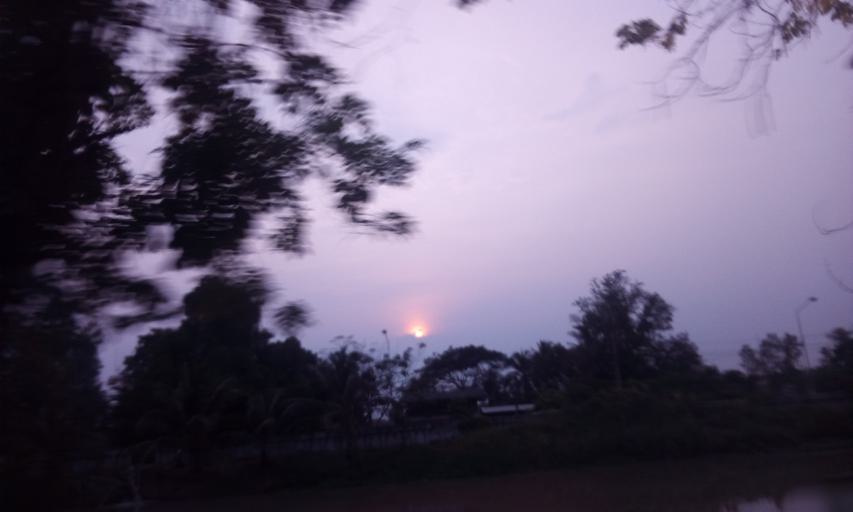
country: TH
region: Pathum Thani
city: Ban Lam Luk Ka
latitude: 13.9889
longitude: 100.8952
